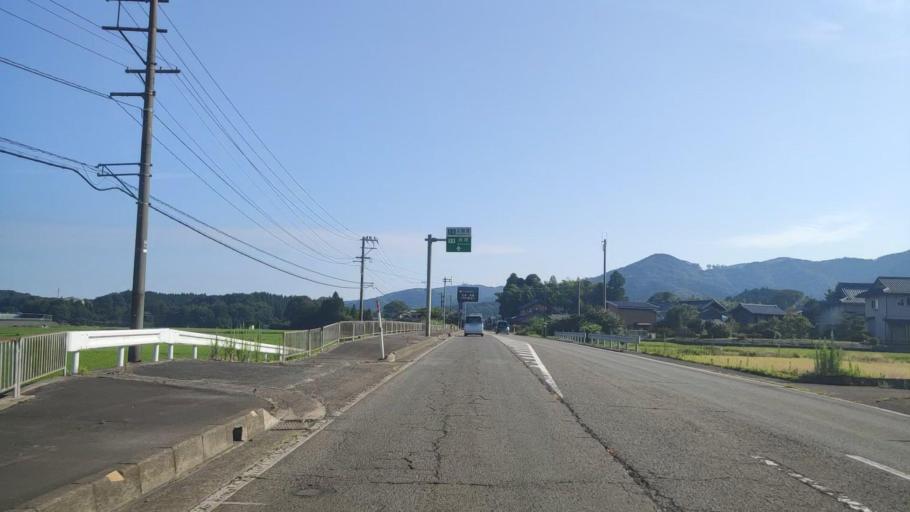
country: JP
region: Fukui
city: Maruoka
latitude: 36.2294
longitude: 136.2856
